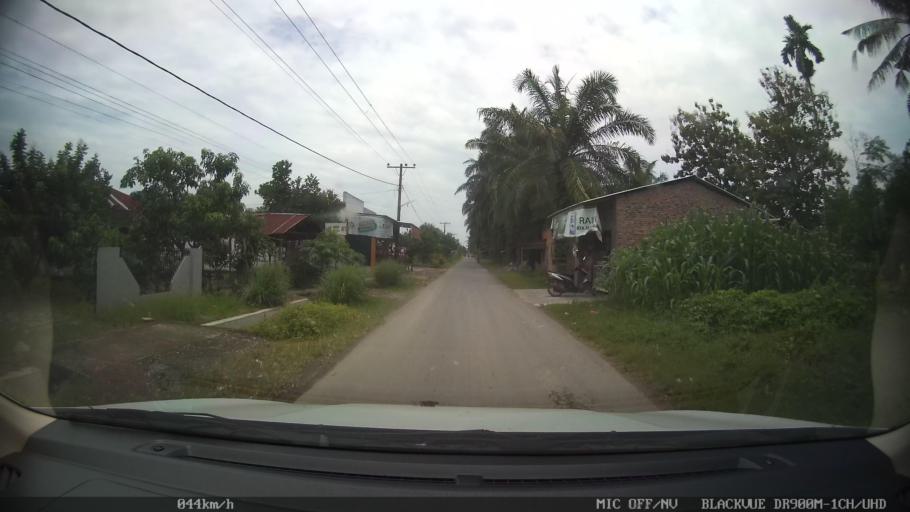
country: ID
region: North Sumatra
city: Sunggal
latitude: 3.6334
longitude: 98.5687
